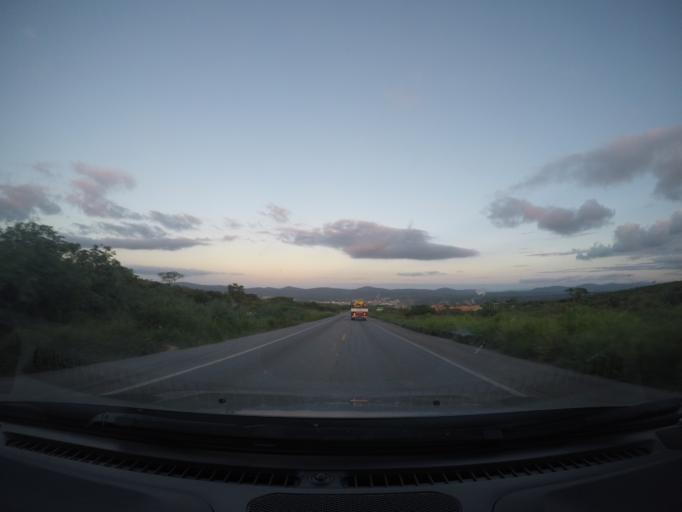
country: BR
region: Bahia
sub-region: Seabra
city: Seabra
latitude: -12.4322
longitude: -41.8065
